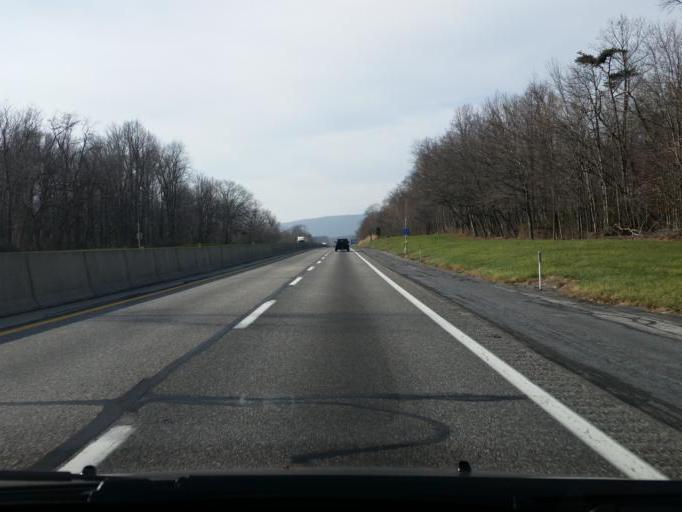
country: US
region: Pennsylvania
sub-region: Cumberland County
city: Shippensburg
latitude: 40.1684
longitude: -77.5792
